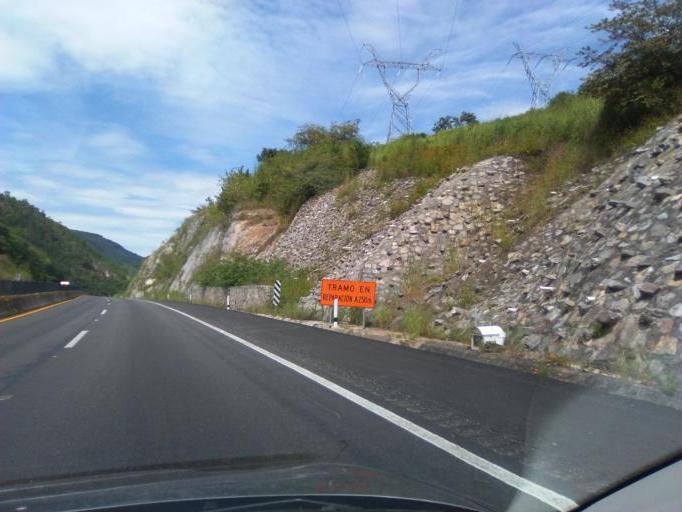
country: MX
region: Guerrero
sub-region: Chilpancingo de los Bravo
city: Acahuizotla
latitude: 17.3498
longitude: -99.4781
